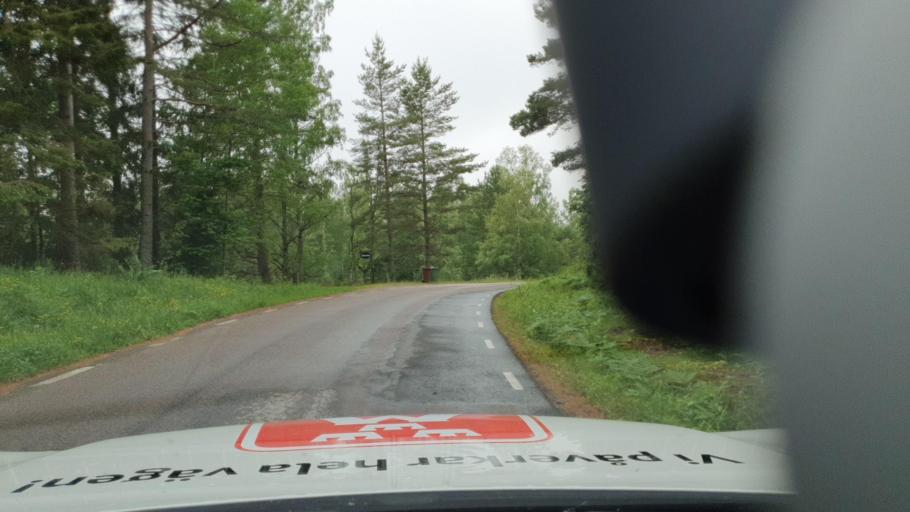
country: SE
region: Vaestra Goetaland
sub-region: Gullspangs Kommun
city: Gullspang
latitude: 59.0317
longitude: 14.1632
